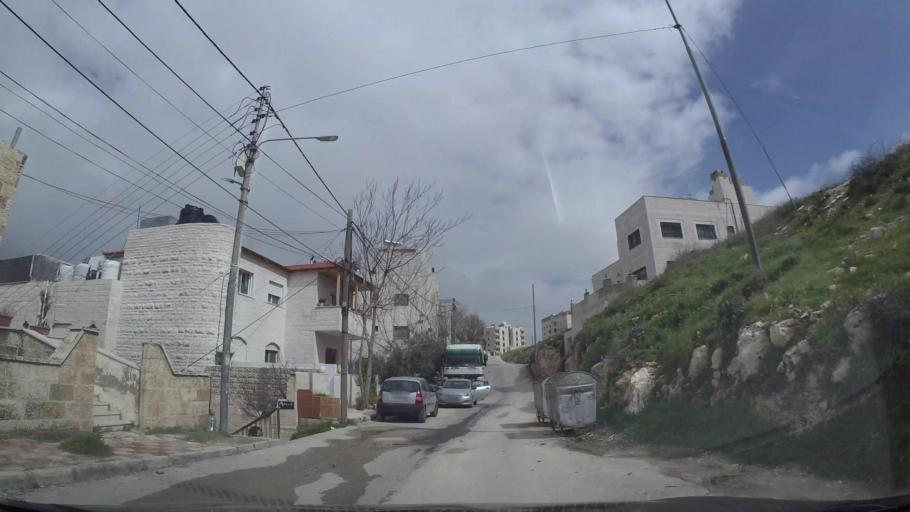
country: JO
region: Amman
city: Wadi as Sir
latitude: 31.9514
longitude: 35.8270
